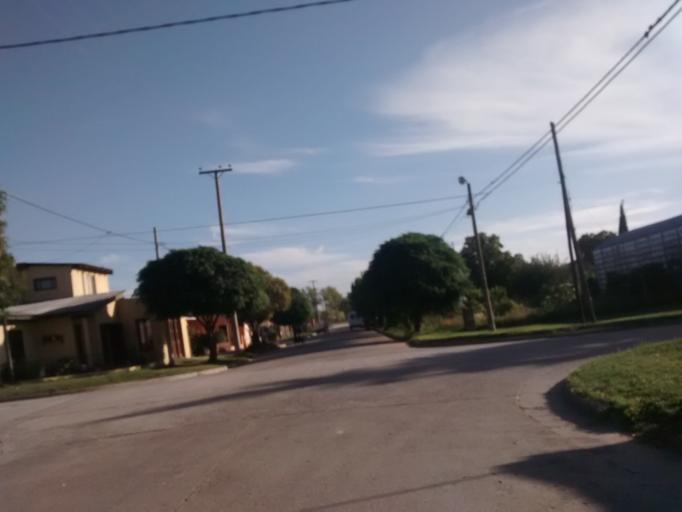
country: AR
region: Buenos Aires
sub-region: Partido de Loberia
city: Loberia
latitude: -38.1697
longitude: -58.7814
